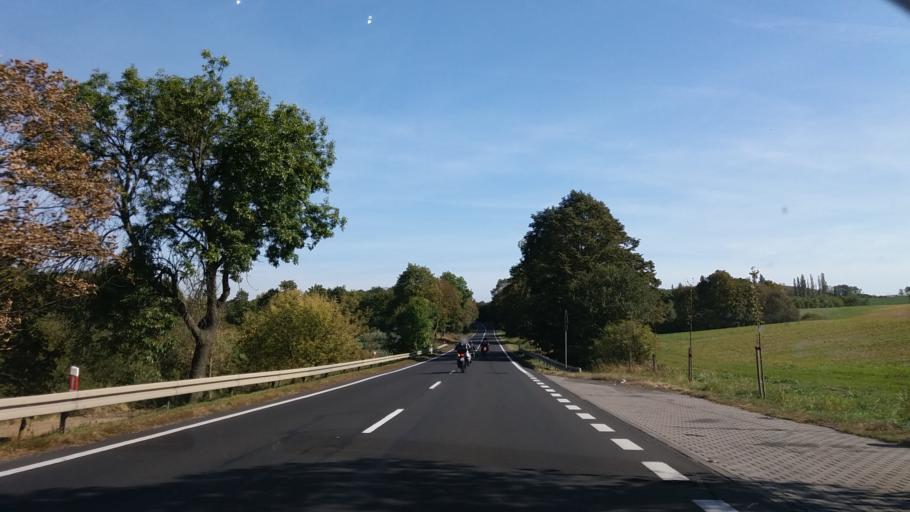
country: PL
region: Greater Poland Voivodeship
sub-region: Powiat miedzychodzki
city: Miedzychod
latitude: 52.5636
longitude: 15.9872
